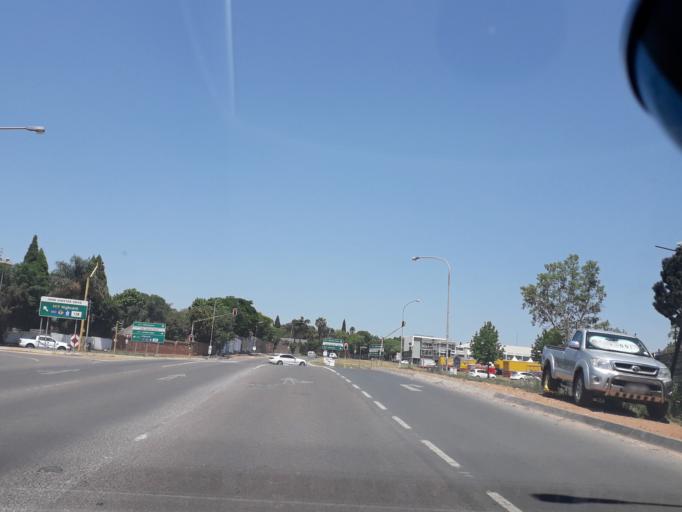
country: ZA
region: Gauteng
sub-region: City of Tshwane Metropolitan Municipality
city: Centurion
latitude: -25.8627
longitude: 28.1873
